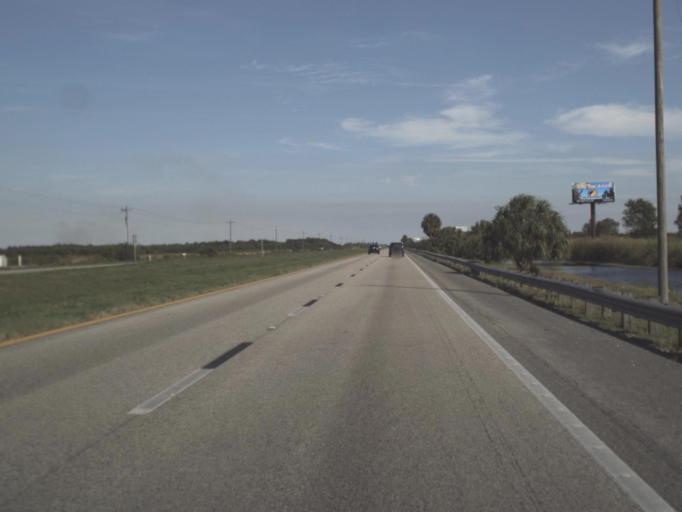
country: US
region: Florida
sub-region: Glades County
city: Moore Haven
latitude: 26.7536
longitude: -81.0479
